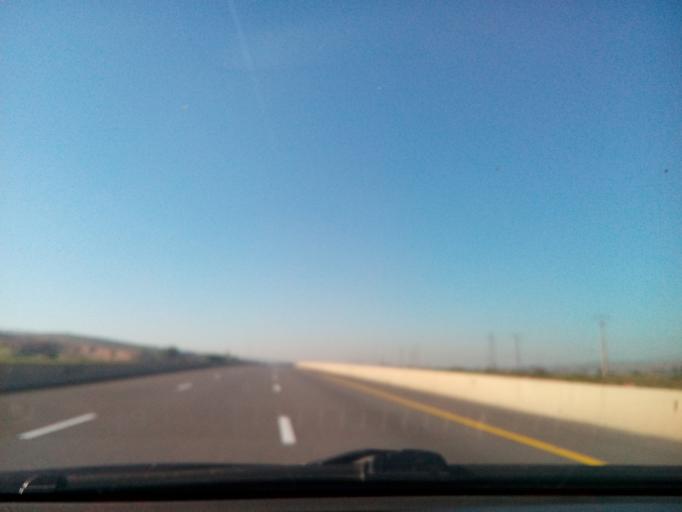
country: DZ
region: Chlef
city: Boukadir
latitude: 36.0381
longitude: 1.0872
